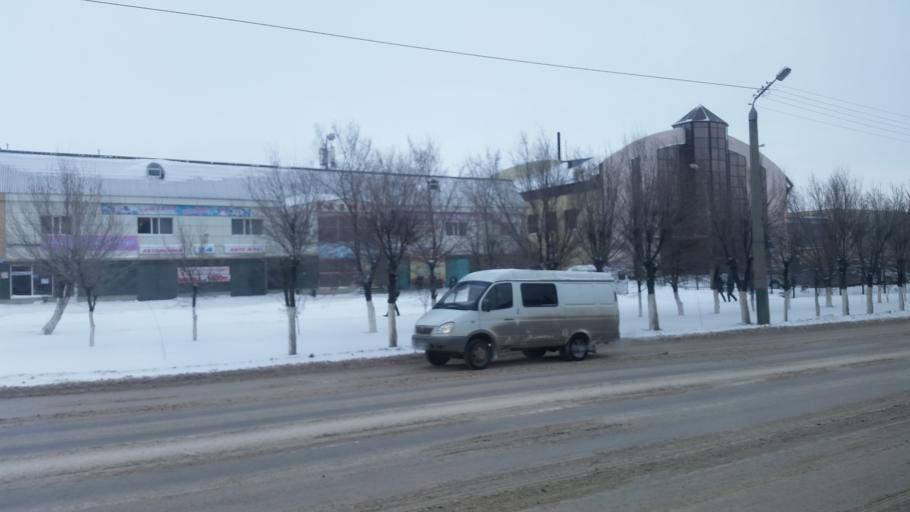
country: KZ
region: Qaraghandy
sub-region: Qaraghandy Qalasy
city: Karagandy
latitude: 49.7744
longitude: 73.1491
